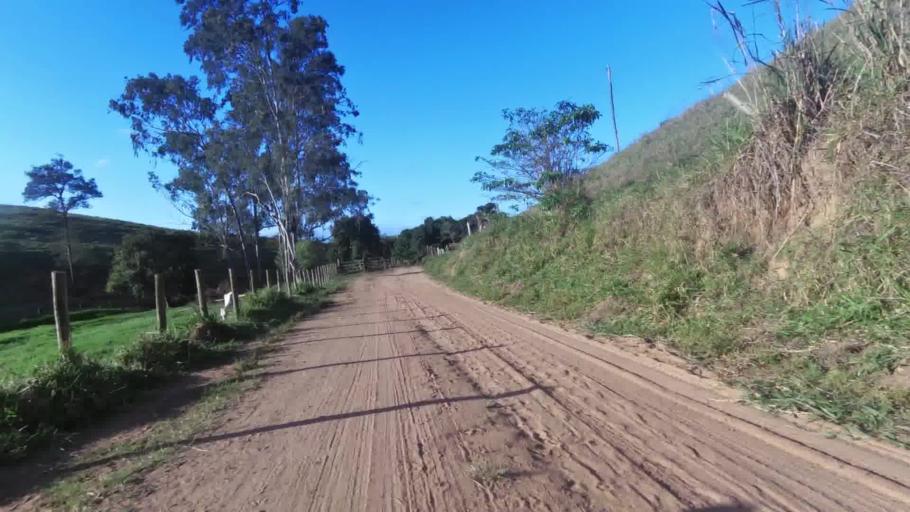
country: BR
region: Espirito Santo
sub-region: Marataizes
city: Marataizes
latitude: -21.1473
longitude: -41.0299
